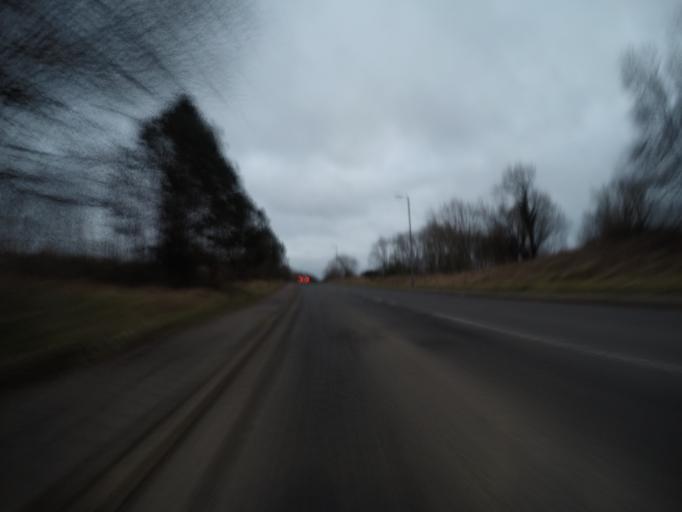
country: GB
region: Scotland
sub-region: North Ayrshire
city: Kilwinning
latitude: 55.6454
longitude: -4.6958
